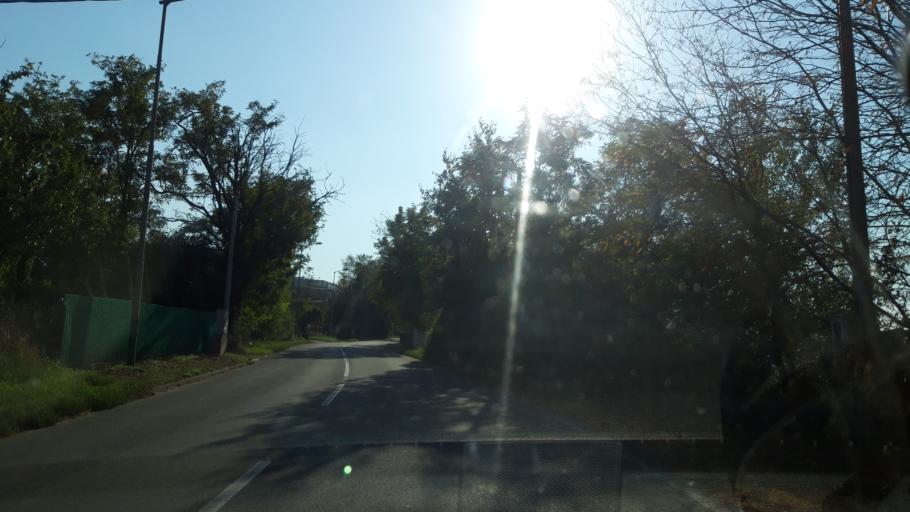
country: RS
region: Autonomna Pokrajina Vojvodina
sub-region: Juznobacki Okrug
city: Petrovaradin
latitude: 45.2357
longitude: 19.8622
